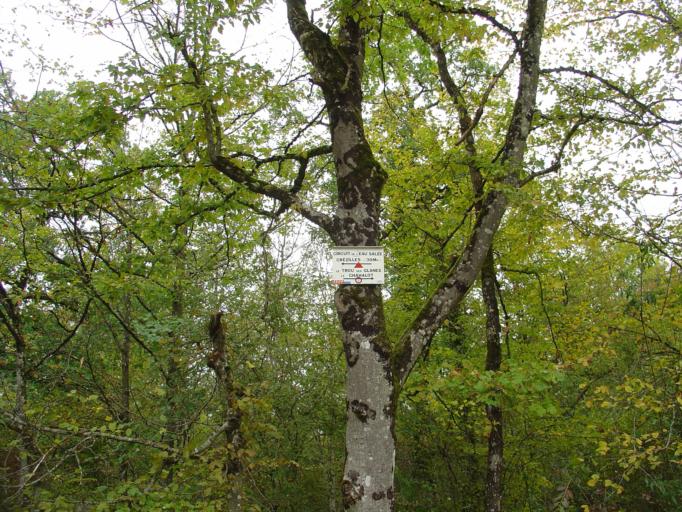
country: FR
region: Lorraine
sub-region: Departement de Meurthe-et-Moselle
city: Colombey-les-Belles
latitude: 48.5850
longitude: 5.9033
